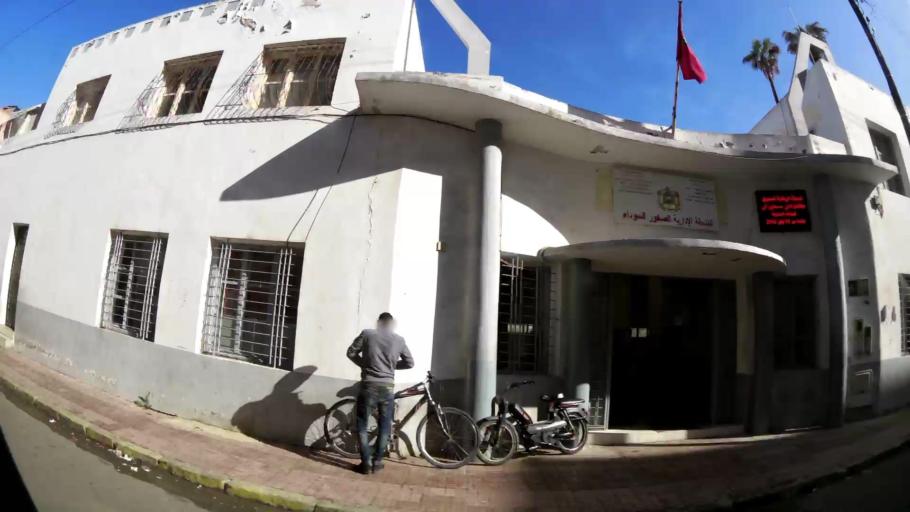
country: MA
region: Grand Casablanca
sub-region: Casablanca
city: Casablanca
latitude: 33.5990
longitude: -7.5832
